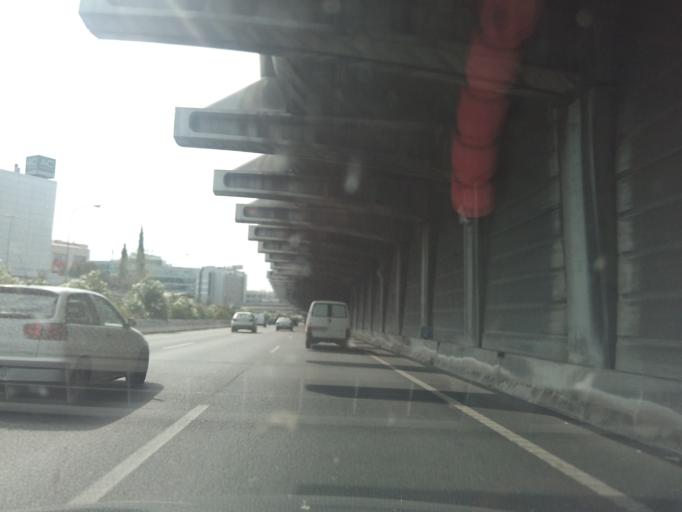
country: ES
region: Madrid
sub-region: Provincia de Madrid
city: Hortaleza
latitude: 40.4753
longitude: -3.6359
